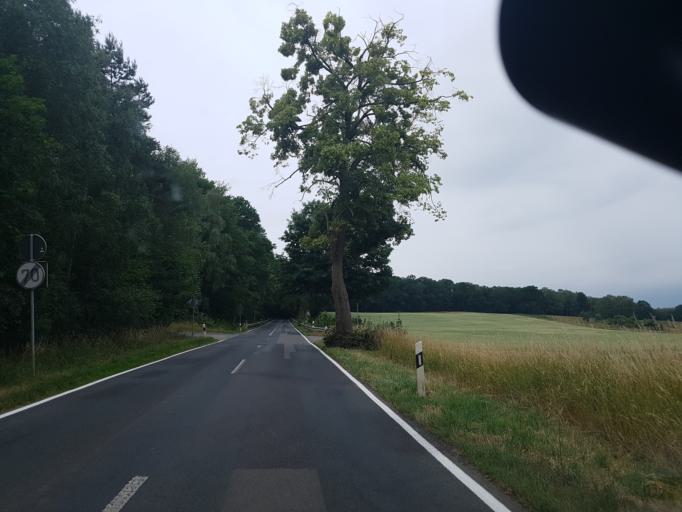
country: DE
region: Brandenburg
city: Lebusa
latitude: 51.7912
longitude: 13.4082
